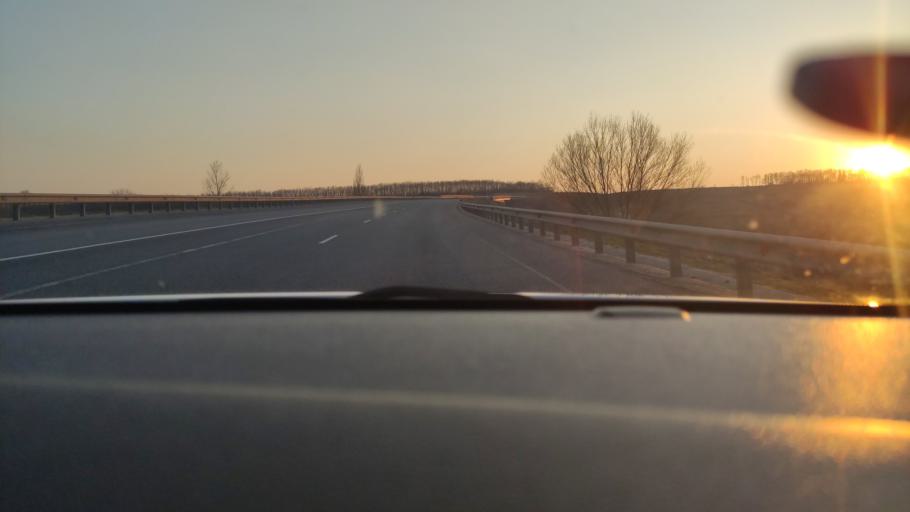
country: RU
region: Voronezj
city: Kolodeznyy
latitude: 51.3298
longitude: 39.1603
